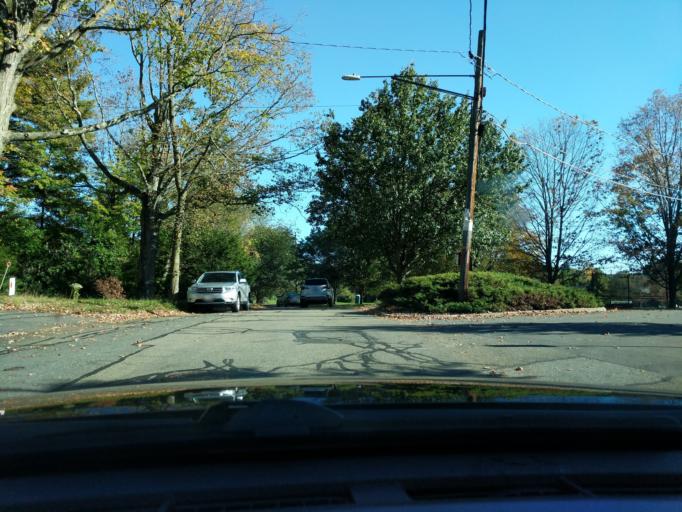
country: US
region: Massachusetts
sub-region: Norfolk County
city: Wellesley
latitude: 42.3318
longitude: -71.2603
